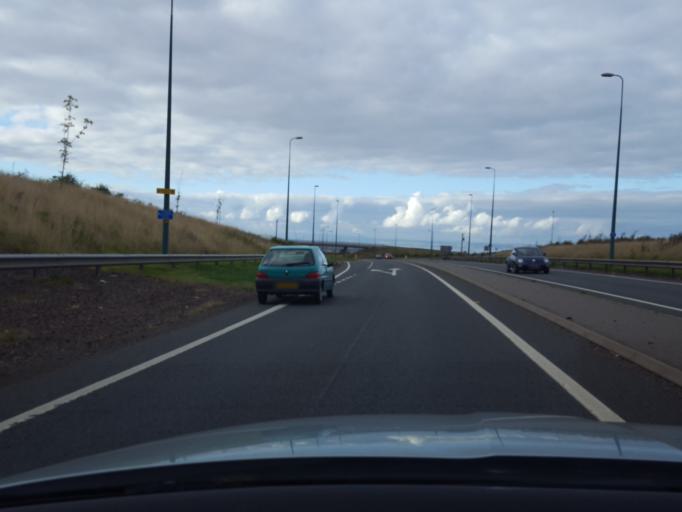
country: GB
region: Scotland
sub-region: Fife
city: Pathhead
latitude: 55.8920
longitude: -2.9985
